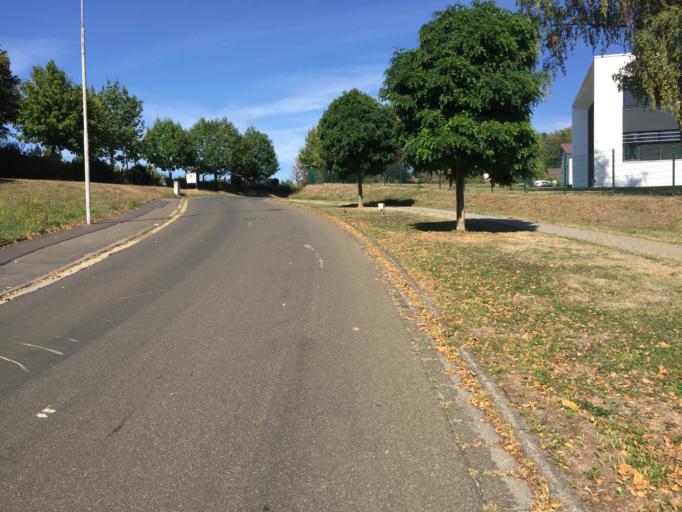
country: DE
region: Hesse
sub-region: Regierungsbezirk Giessen
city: Reiskirchen
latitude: 50.5983
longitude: 8.8574
